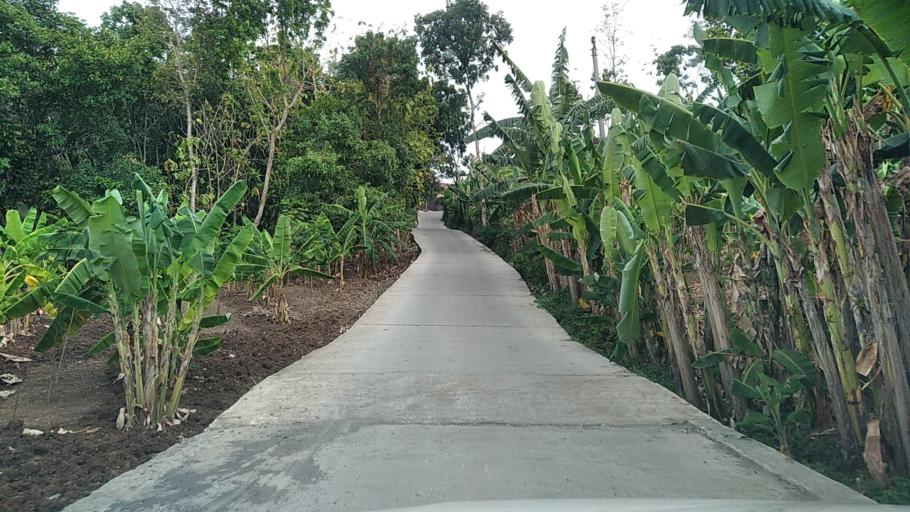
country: ID
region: Central Java
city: Semarang
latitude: -6.9977
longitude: 110.3075
